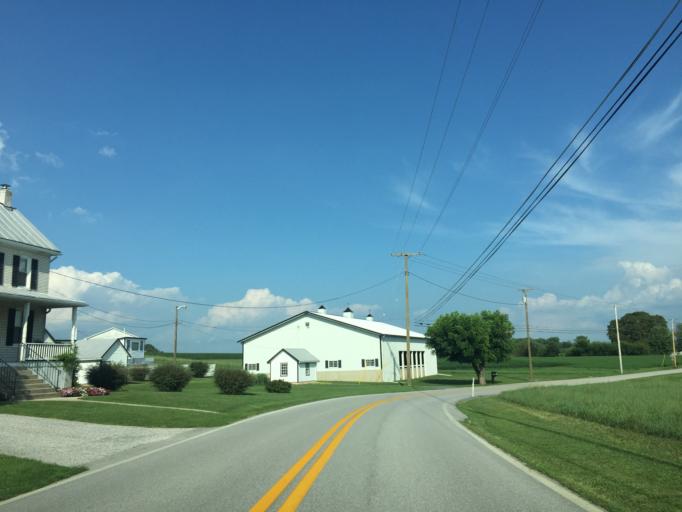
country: US
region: Maryland
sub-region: Carroll County
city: Manchester
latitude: 39.6529
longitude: -76.8516
